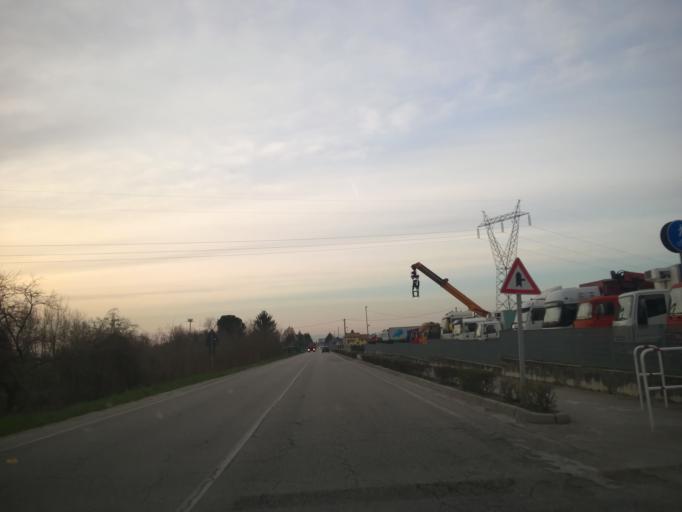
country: IT
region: Veneto
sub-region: Provincia di Vicenza
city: Centrale
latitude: 45.7314
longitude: 11.4648
